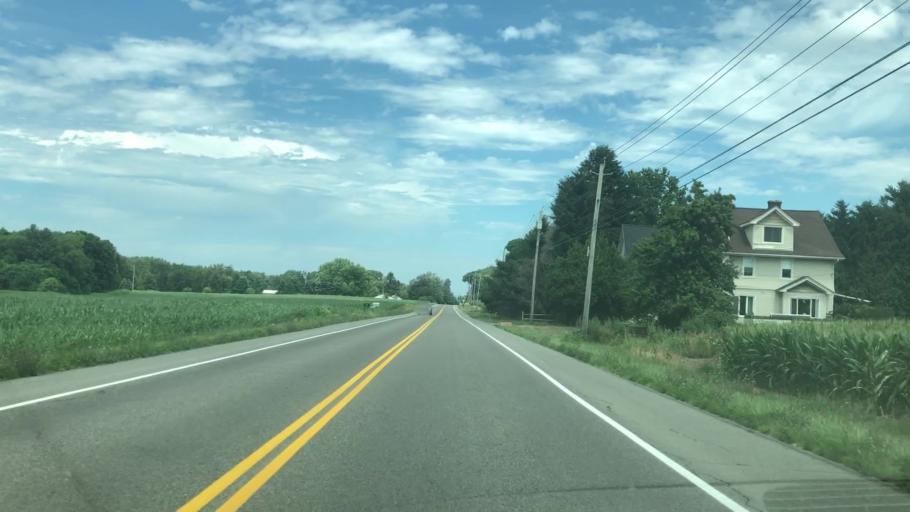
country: US
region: New York
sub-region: Monroe County
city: Webster
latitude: 43.2074
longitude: -77.4004
